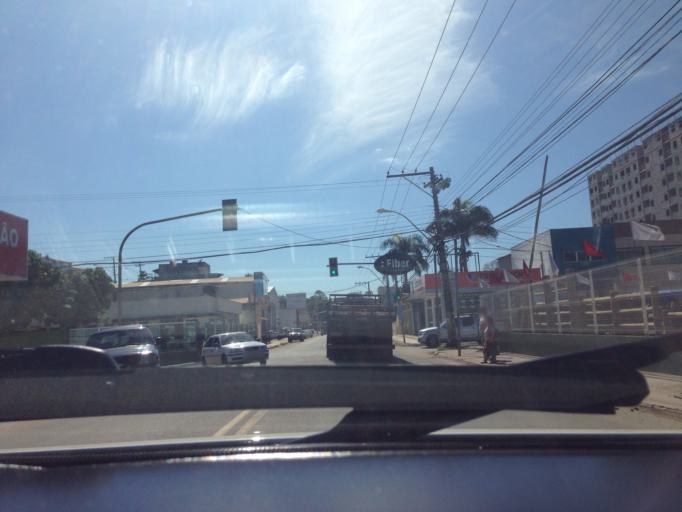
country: BR
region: Espirito Santo
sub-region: Guarapari
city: Guarapari
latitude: -20.6408
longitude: -40.4841
